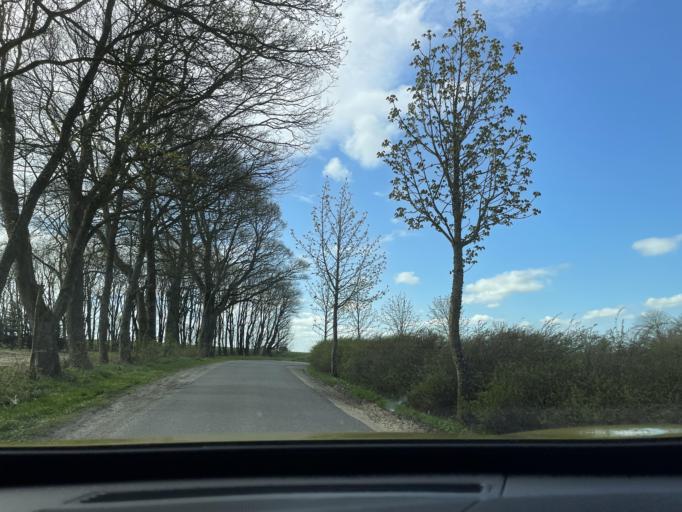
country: DK
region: Central Jutland
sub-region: Favrskov Kommune
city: Hinnerup
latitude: 56.2984
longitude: 10.1071
